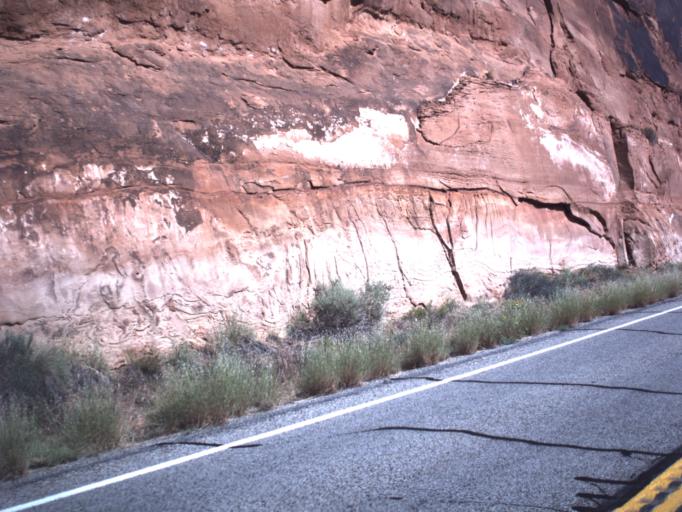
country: US
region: Utah
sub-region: Grand County
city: Moab
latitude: 38.5350
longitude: -109.6270
